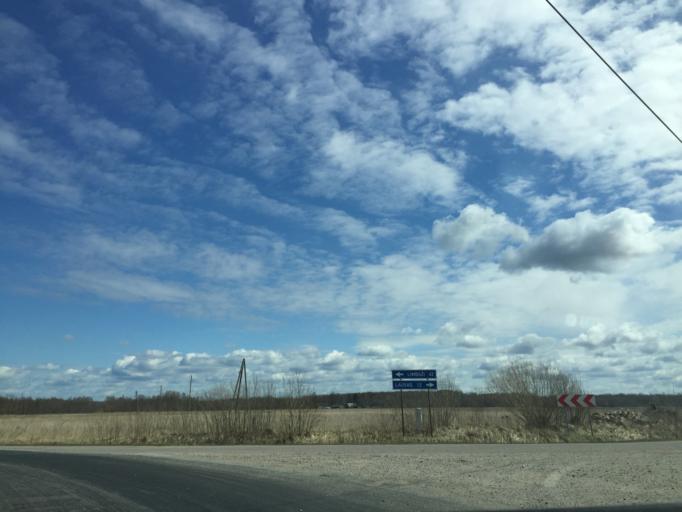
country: LV
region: Salacgrivas
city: Salacgriva
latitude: 57.7443
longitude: 24.3954
